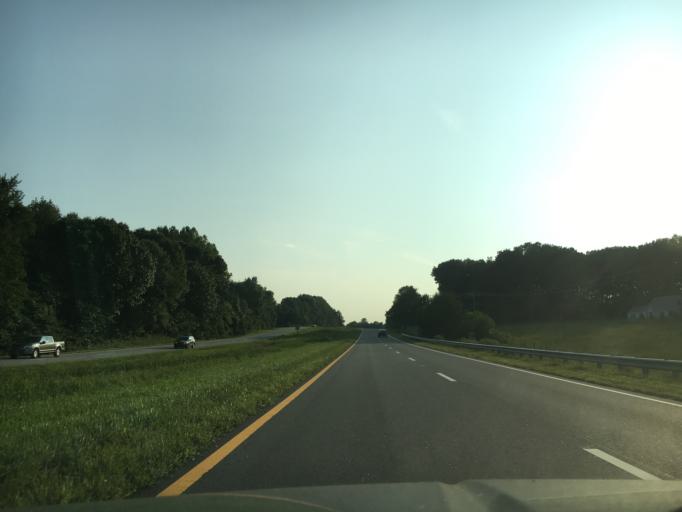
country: US
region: Virginia
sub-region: Prince Edward County
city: Hampden Sydney
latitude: 37.2694
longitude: -78.6452
